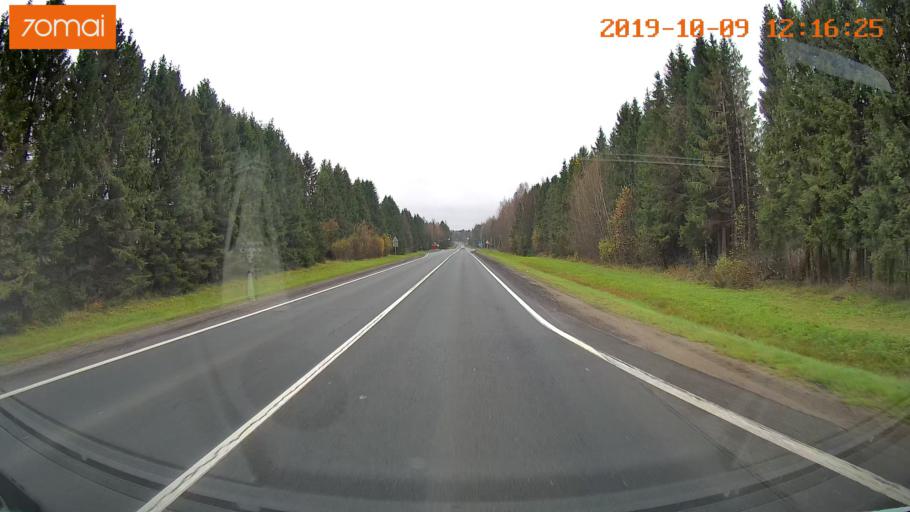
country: RU
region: Jaroslavl
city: Prechistoye
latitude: 58.4689
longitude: 40.3212
